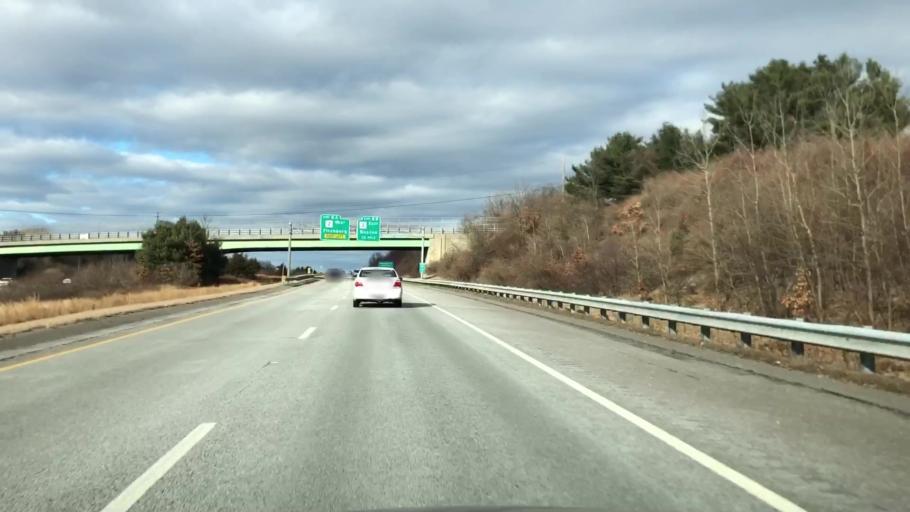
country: US
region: Massachusetts
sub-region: Worcester County
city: Leominster
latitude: 42.5067
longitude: -71.7206
